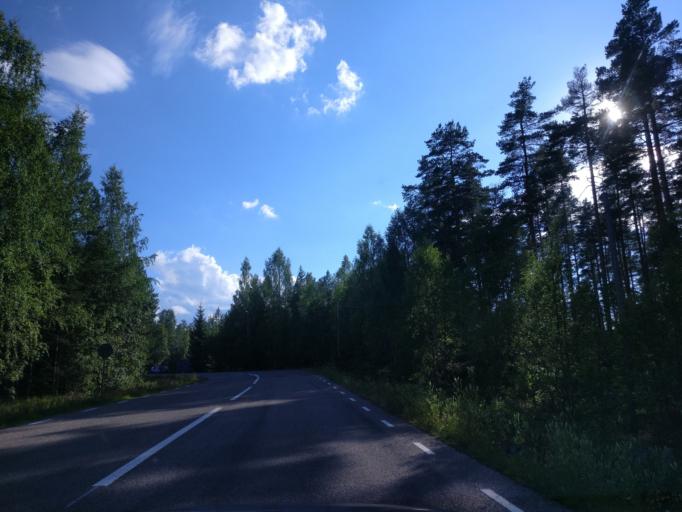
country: SE
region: Dalarna
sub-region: Ludvika Kommun
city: Ludvika
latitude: 60.2960
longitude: 15.2162
